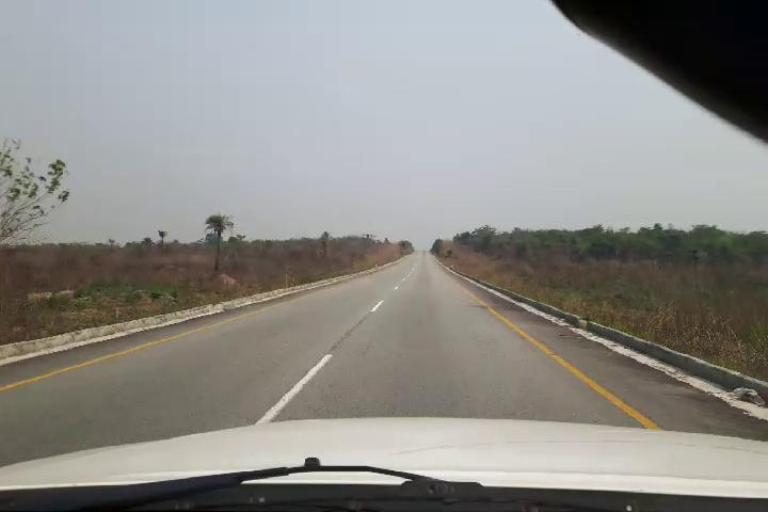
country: SL
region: Southern Province
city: Largo
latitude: 8.2322
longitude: -12.0803
